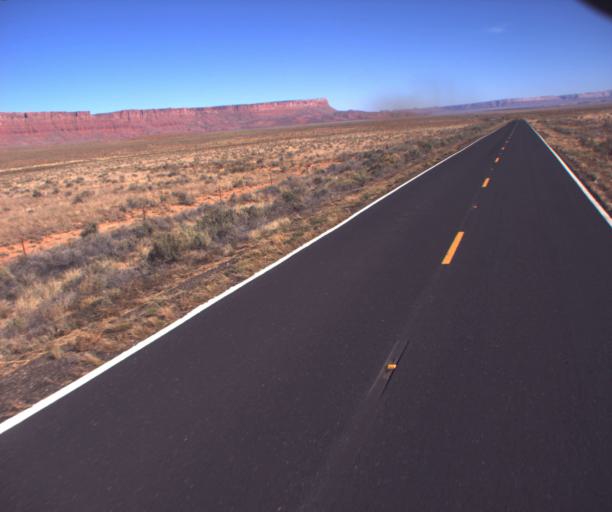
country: US
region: Arizona
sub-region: Coconino County
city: Fredonia
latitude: 36.7192
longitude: -112.0069
